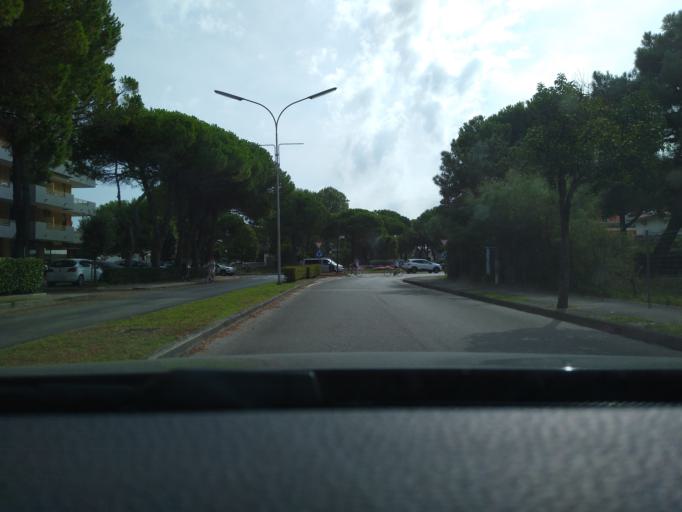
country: IT
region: Veneto
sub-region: Provincia di Venezia
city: Bibione
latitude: 45.6429
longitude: 13.0538
